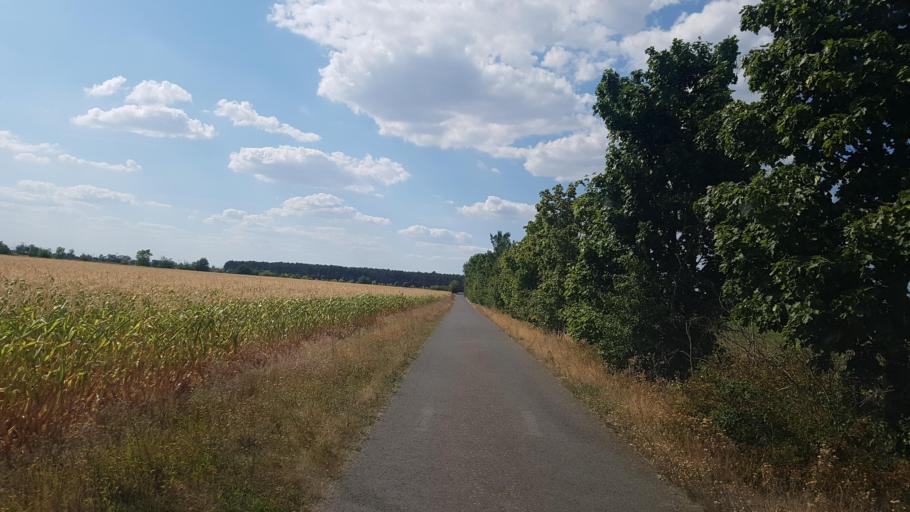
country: DE
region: Saxony-Anhalt
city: Elster
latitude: 51.8395
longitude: 12.8148
